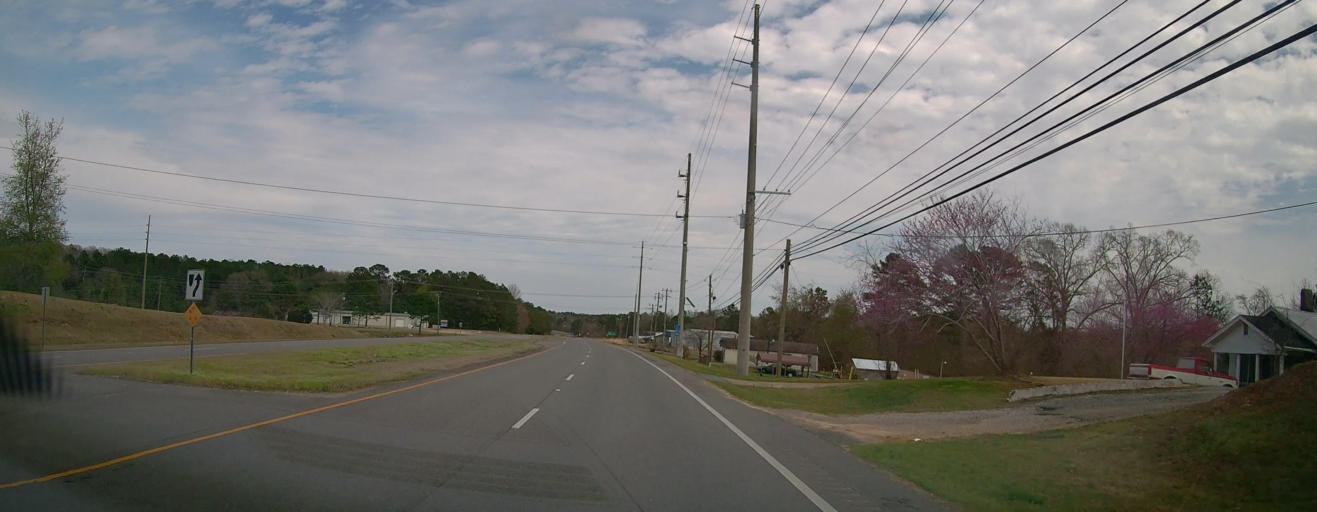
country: US
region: Alabama
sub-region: Marion County
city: Winfield
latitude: 33.9295
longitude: -87.7735
